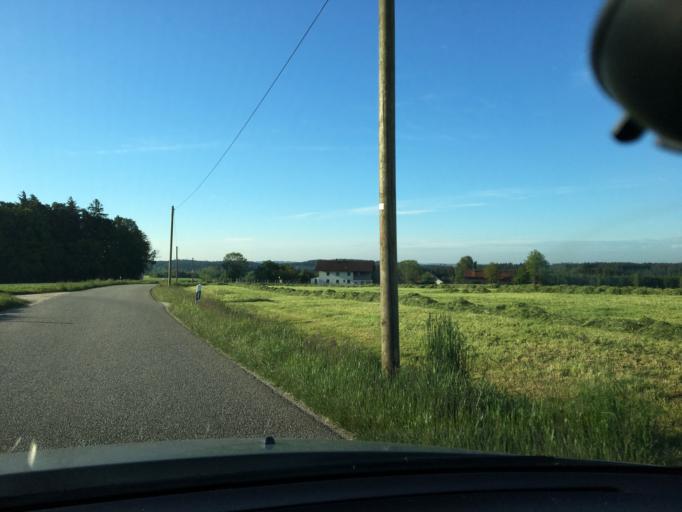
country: DE
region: Bavaria
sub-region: Lower Bavaria
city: Vilsbiburg
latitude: 48.5123
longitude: 12.3281
